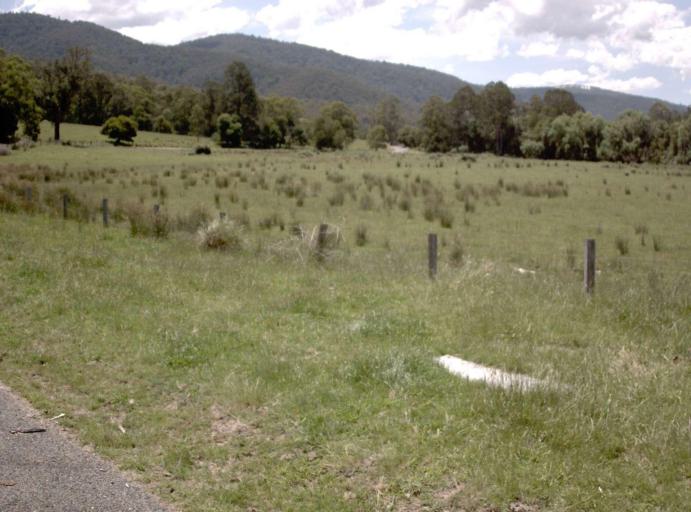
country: AU
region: New South Wales
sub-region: Bombala
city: Bombala
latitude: -37.3907
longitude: 149.0135
